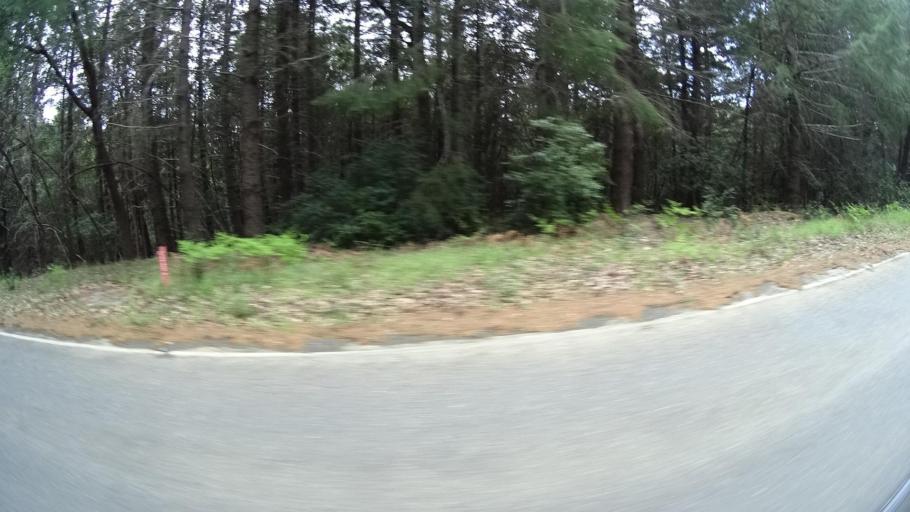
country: US
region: California
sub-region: Humboldt County
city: Redway
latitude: 40.0494
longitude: -124.0106
